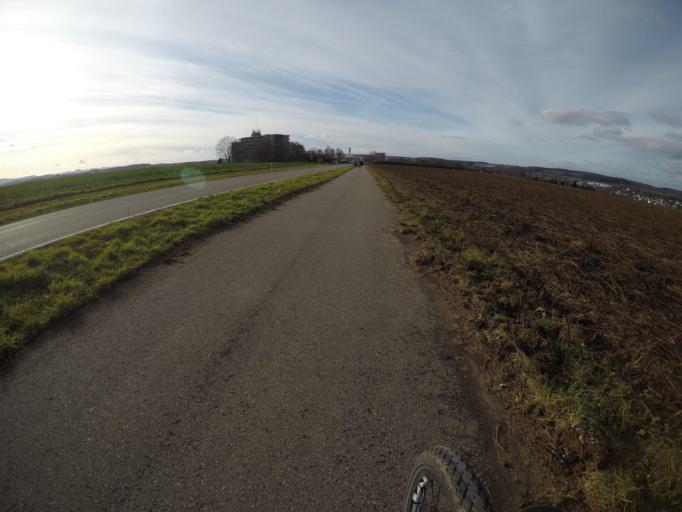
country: DE
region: Baden-Wuerttemberg
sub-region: Regierungsbezirk Stuttgart
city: Oberboihingen
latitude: 48.6306
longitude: 9.3629
